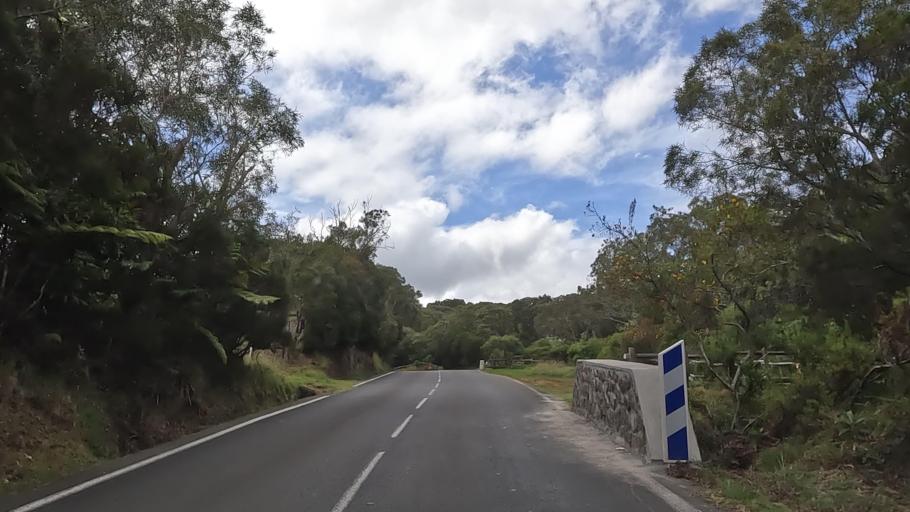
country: RE
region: Reunion
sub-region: Reunion
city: Le Tampon
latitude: -21.2401
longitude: 55.5857
